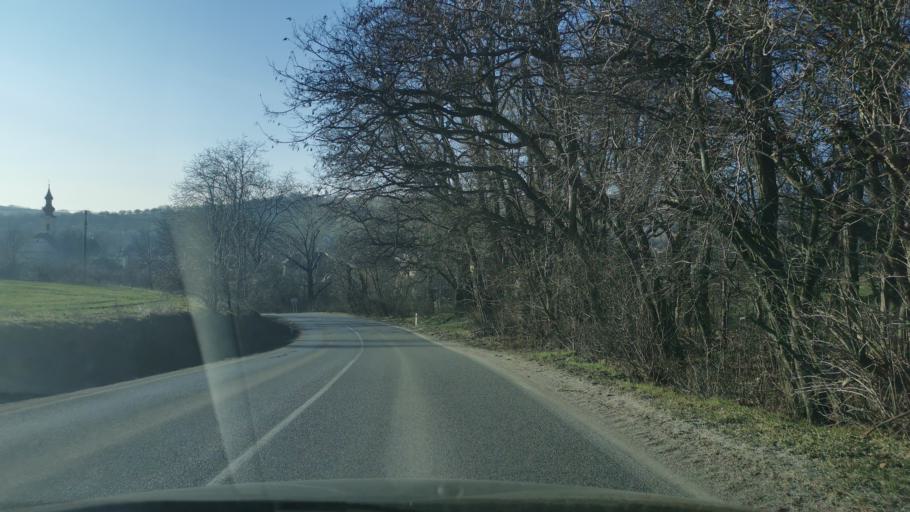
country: SK
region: Trnavsky
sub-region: Okres Senica
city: Senica
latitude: 48.7328
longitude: 17.4143
